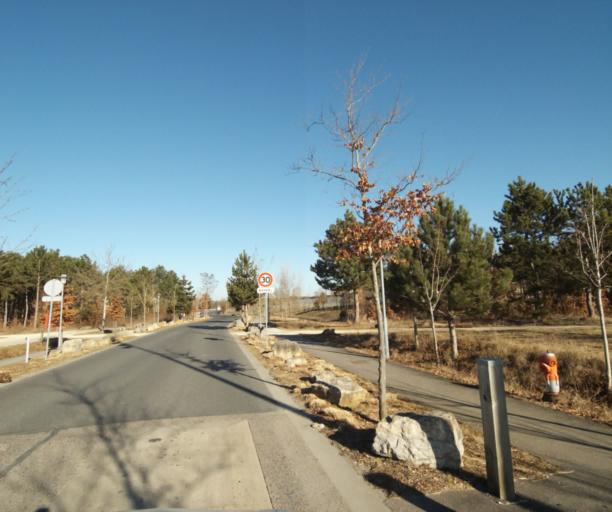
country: FR
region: Lorraine
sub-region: Departement de Meurthe-et-Moselle
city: Maxeville
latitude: 48.7047
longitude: 6.1500
